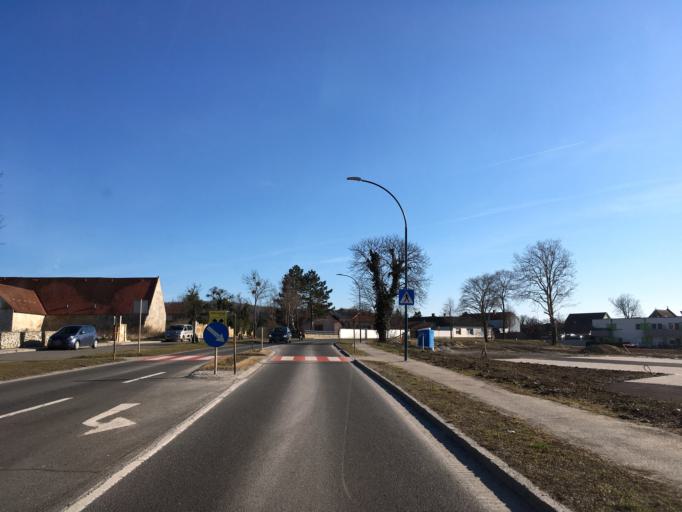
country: AT
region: Burgenland
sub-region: Eisenstadt-Umgebung
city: Hornstein
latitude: 47.8838
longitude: 16.4402
